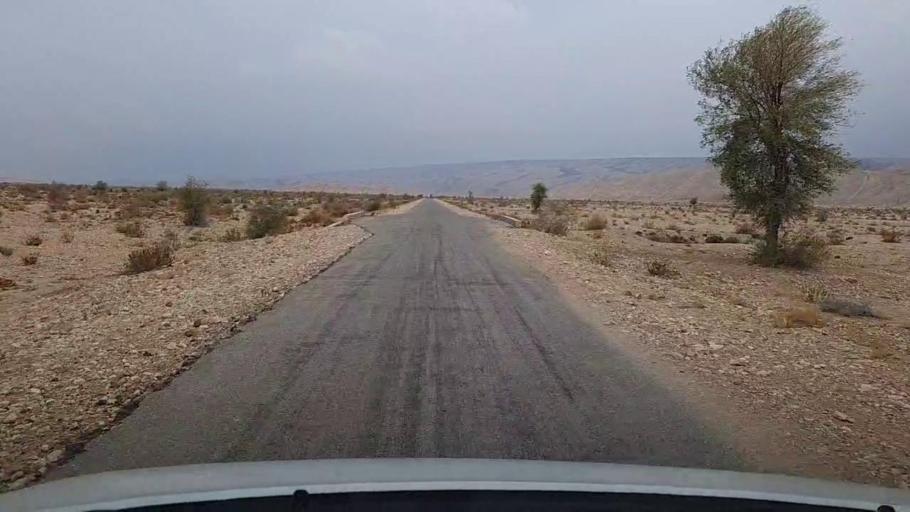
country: PK
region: Sindh
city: Sehwan
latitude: 26.2537
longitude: 67.7200
